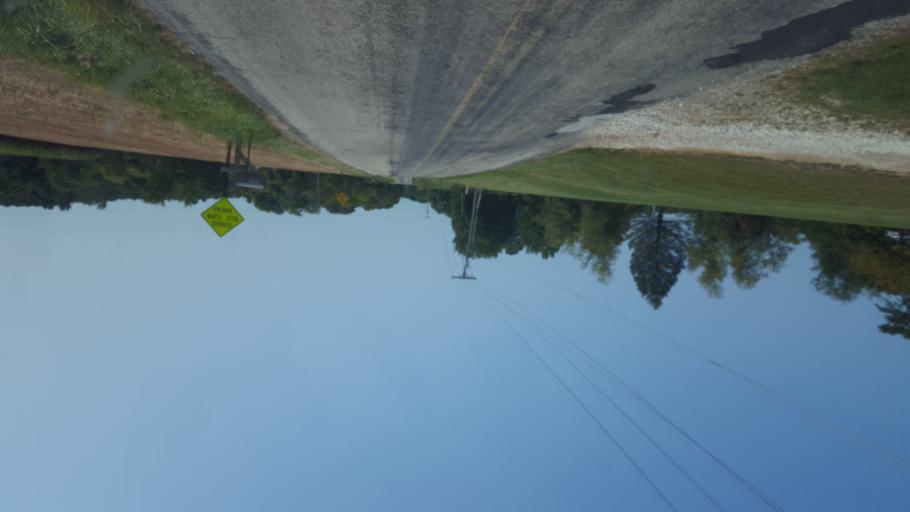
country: US
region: Ohio
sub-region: Sandusky County
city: Bellville
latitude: 40.5651
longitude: -82.5494
